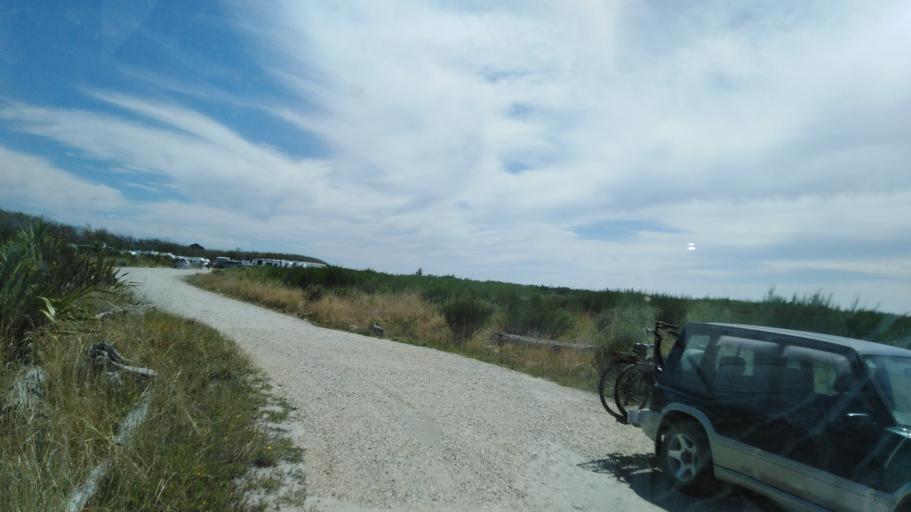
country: NZ
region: West Coast
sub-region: Buller District
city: Westport
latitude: -41.7341
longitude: 171.6053
